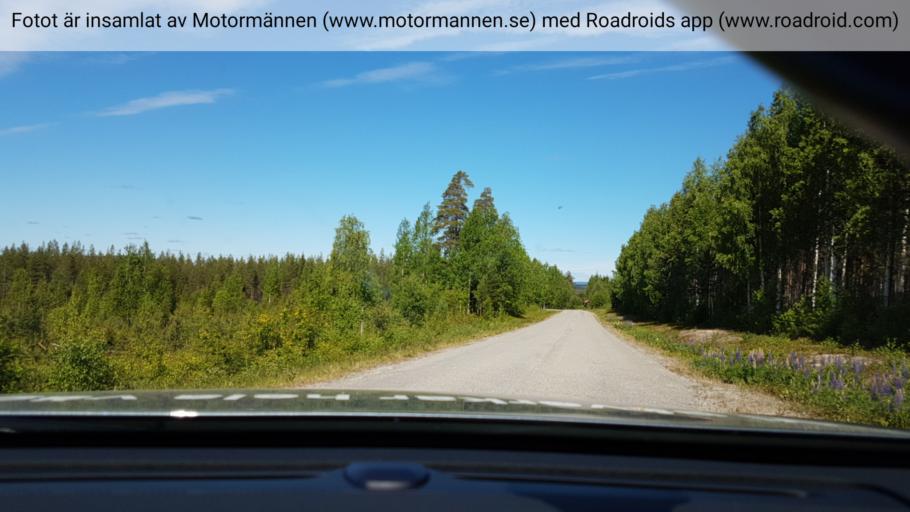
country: SE
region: Vaesterbotten
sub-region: Lycksele Kommun
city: Lycksele
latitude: 64.0783
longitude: 18.3523
